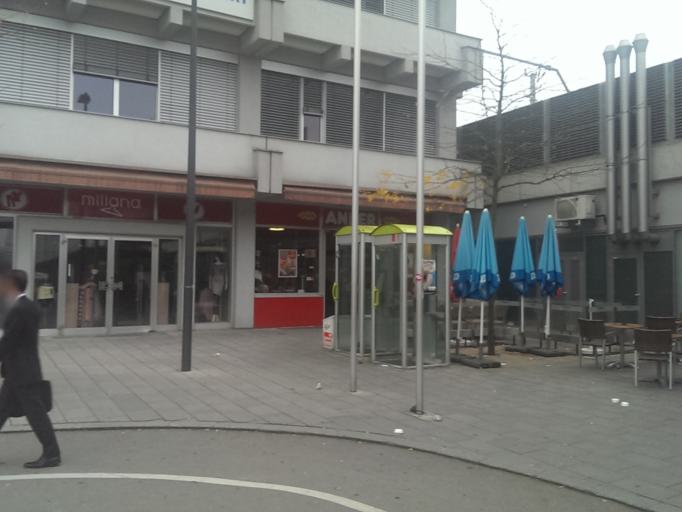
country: AT
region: Lower Austria
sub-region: Sankt Polten Stadt
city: Sankt Poelten
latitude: 48.2089
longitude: 15.6248
